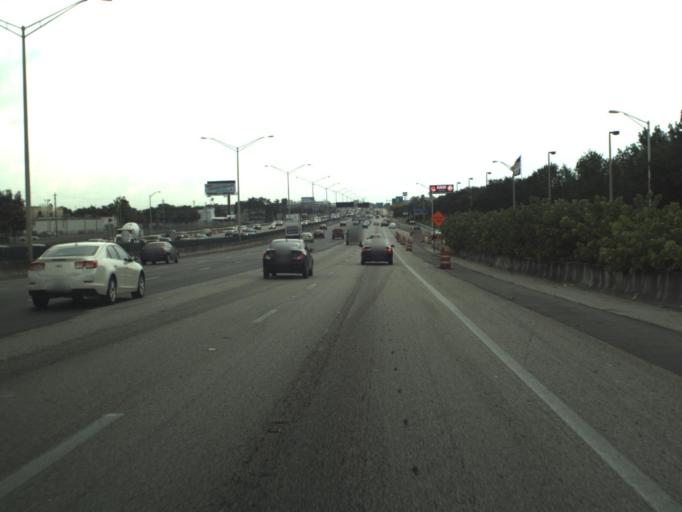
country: US
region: Florida
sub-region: Broward County
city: Dania Beach
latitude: 26.0355
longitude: -80.1638
